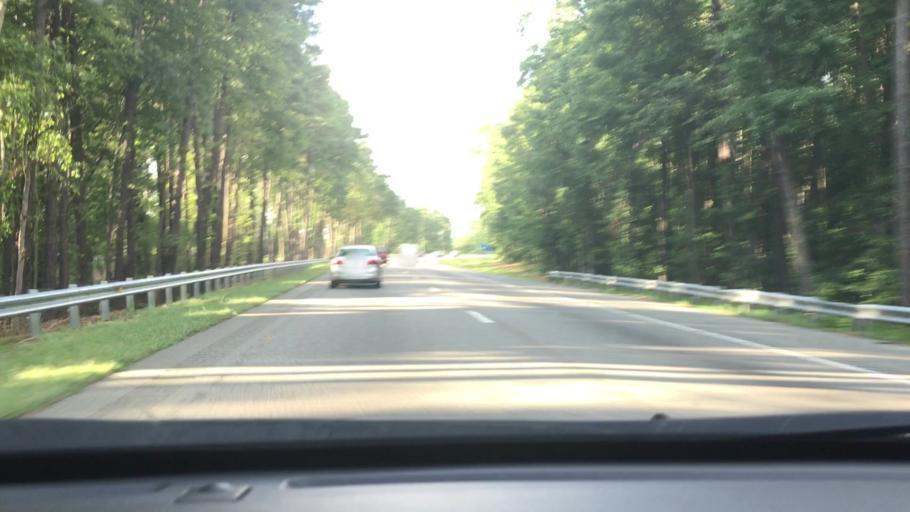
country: US
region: North Carolina
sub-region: Robeson County
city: Saint Pauls
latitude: 34.8269
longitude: -78.9824
